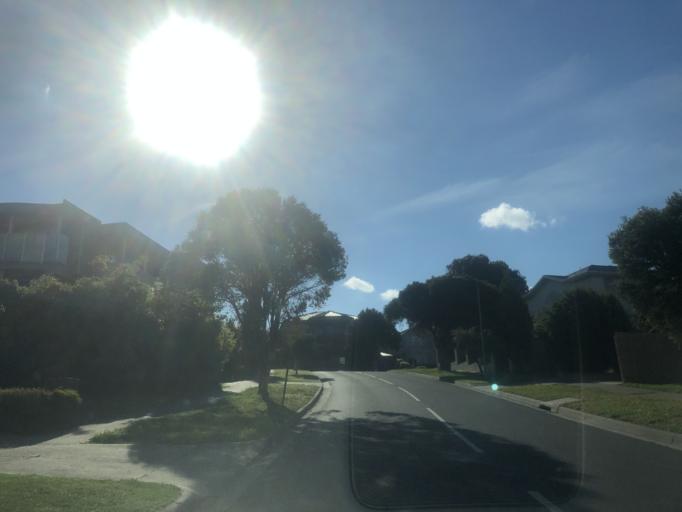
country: AU
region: Victoria
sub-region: Monash
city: Mulgrave
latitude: -37.9159
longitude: 145.1980
